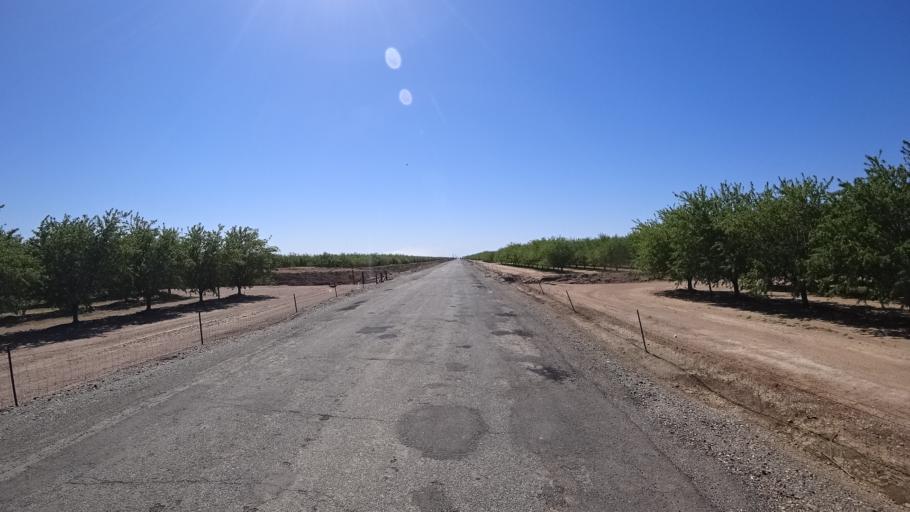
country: US
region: California
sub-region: Glenn County
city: Orland
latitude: 39.6539
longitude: -122.2346
